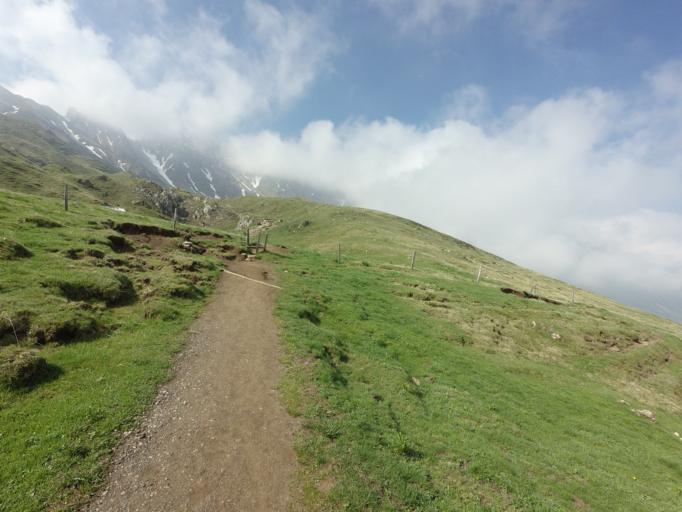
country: IT
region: Trentino-Alto Adige
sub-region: Bolzano
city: Ortisei
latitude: 46.5131
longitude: 11.6347
